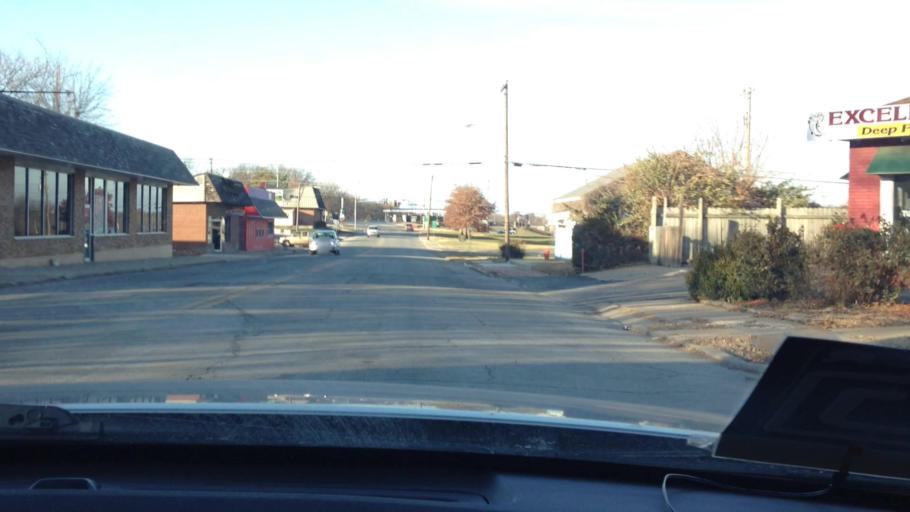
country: US
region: Kansas
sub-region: Leavenworth County
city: Leavenworth
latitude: 39.3264
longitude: -94.9203
